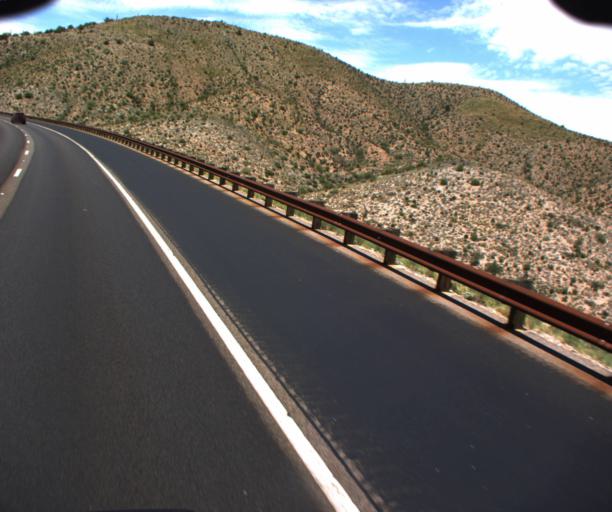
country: US
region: Arizona
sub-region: Pinal County
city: Gold Camp
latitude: 33.2766
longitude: -111.2278
